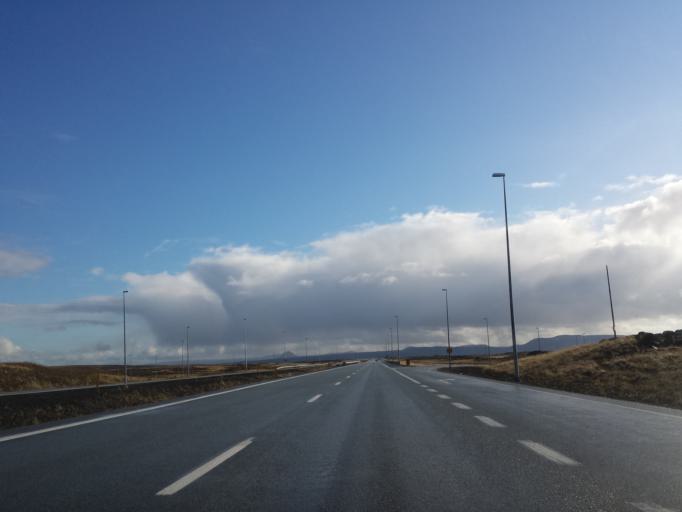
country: IS
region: Southern Peninsula
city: Reykjanesbaer
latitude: 63.9652
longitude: -22.4775
